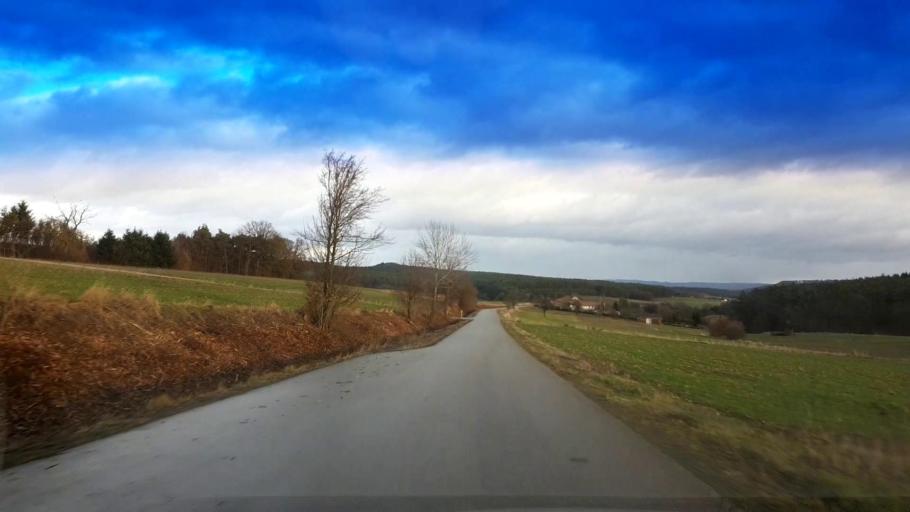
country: DE
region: Bavaria
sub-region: Upper Franconia
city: Lauter
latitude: 49.9798
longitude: 10.7574
